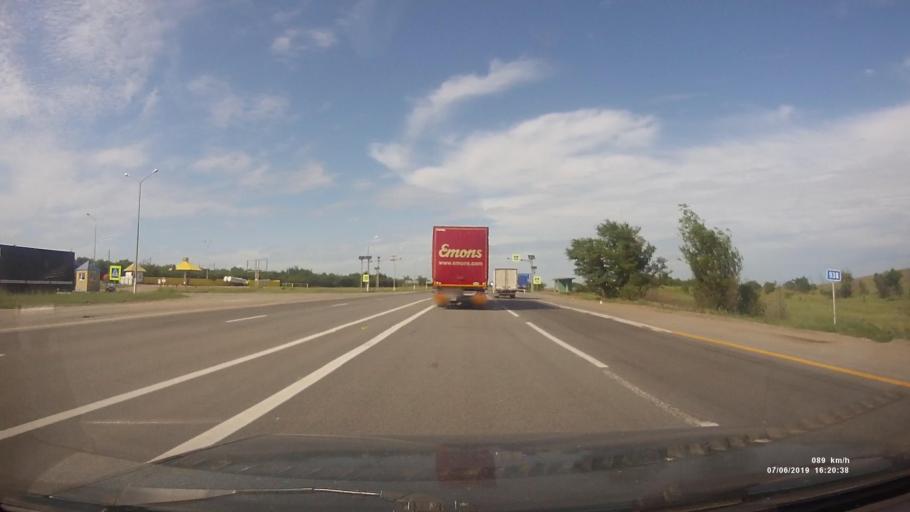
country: RU
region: Rostov
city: Kamensk-Shakhtinskiy
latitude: 48.2452
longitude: 40.2852
